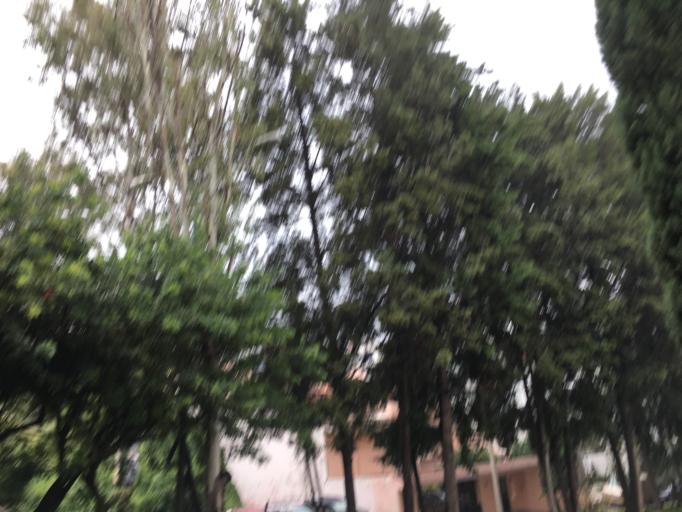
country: MX
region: Mexico City
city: Tlalpan
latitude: 19.2796
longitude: -99.1497
